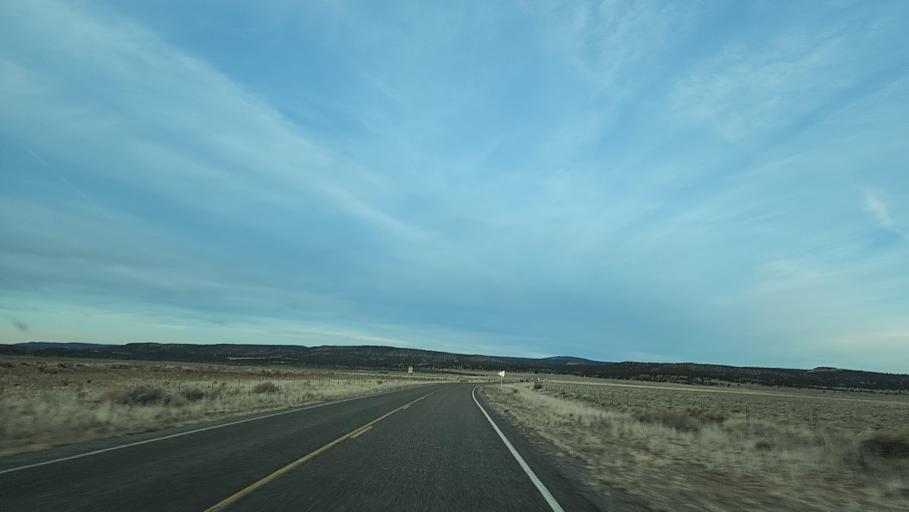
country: US
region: New Mexico
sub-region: Cibola County
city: Grants
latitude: 34.7086
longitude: -108.0082
